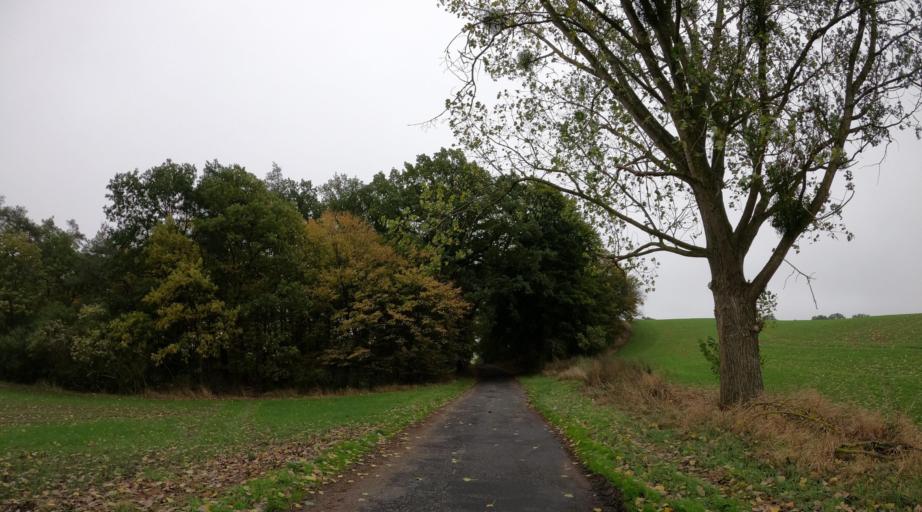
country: PL
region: West Pomeranian Voivodeship
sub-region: Powiat mysliborski
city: Mysliborz
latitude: 52.8993
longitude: 14.7687
